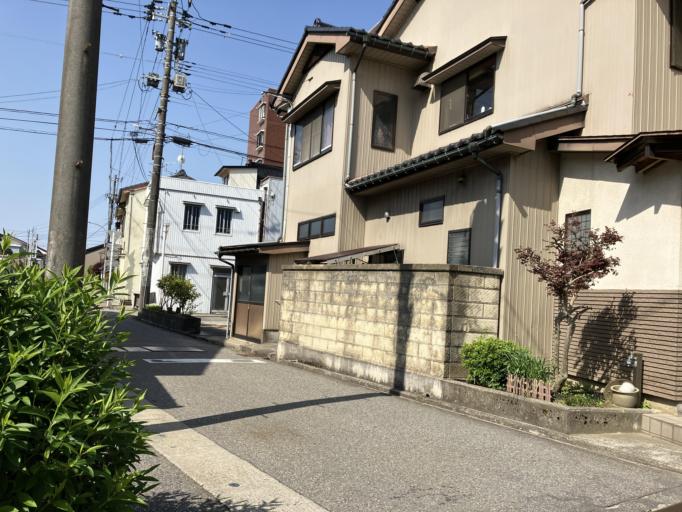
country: JP
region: Toyama
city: Takaoka
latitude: 36.7427
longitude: 137.0216
